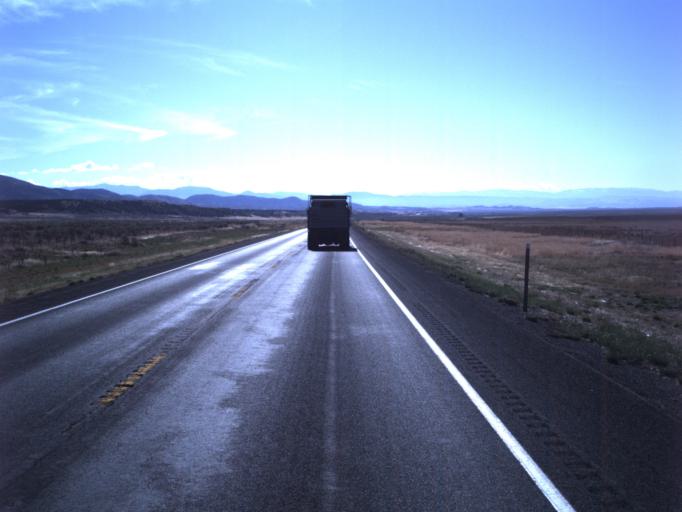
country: US
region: Utah
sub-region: Sanpete County
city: Gunnison
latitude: 39.3136
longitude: -111.9023
